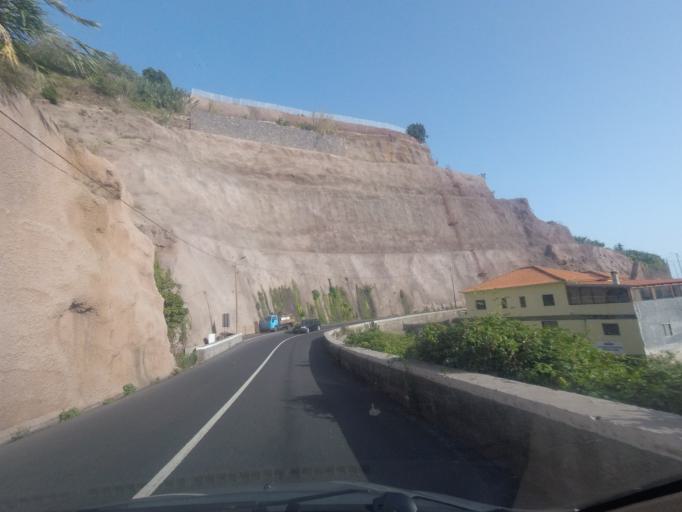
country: PT
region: Madeira
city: Ponta do Sol
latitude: 32.6903
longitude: -17.1072
